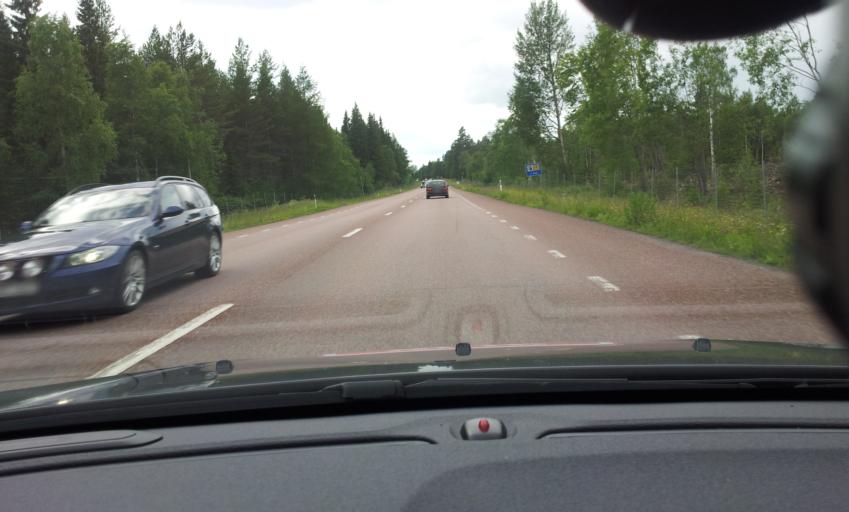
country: SE
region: Jaemtland
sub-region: Krokoms Kommun
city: Krokom
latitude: 63.3259
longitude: 14.3195
